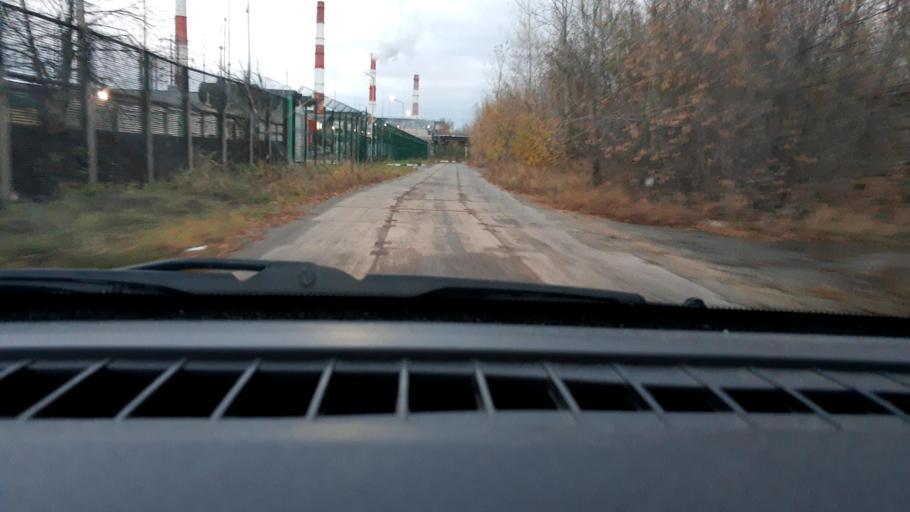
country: RU
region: Nizjnij Novgorod
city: Nizhniy Novgorod
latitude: 56.2380
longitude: 43.9026
